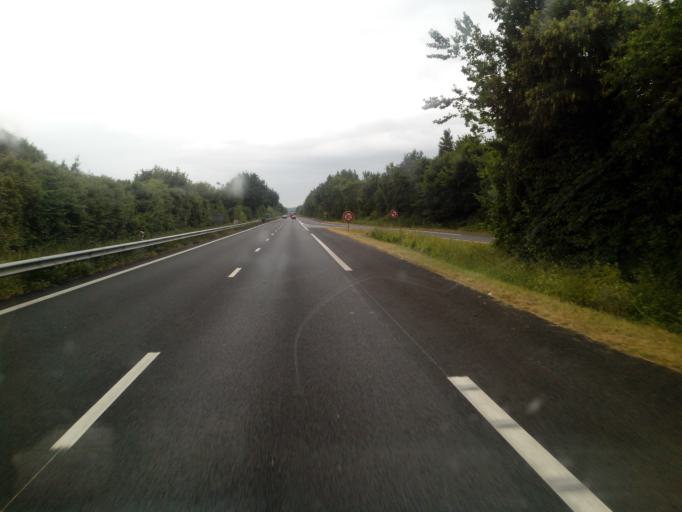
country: FR
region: Pays de la Loire
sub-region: Departement de la Loire-Atlantique
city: Jans
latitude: 47.6257
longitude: -1.6434
